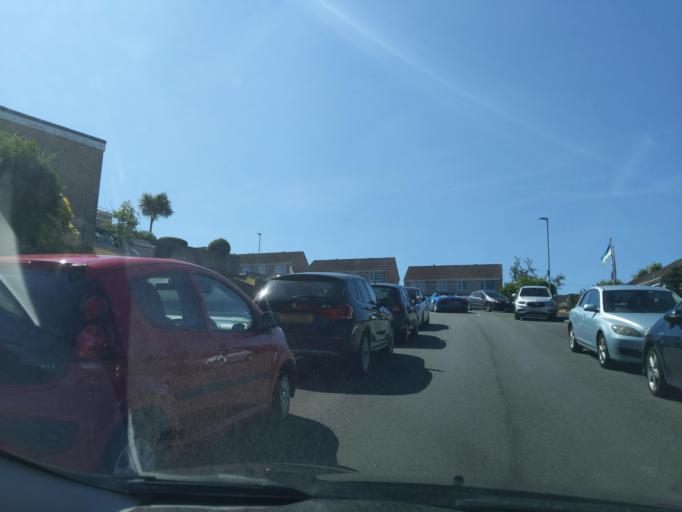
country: GB
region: England
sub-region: Plymouth
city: Plymouth
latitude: 50.4229
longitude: -4.1654
